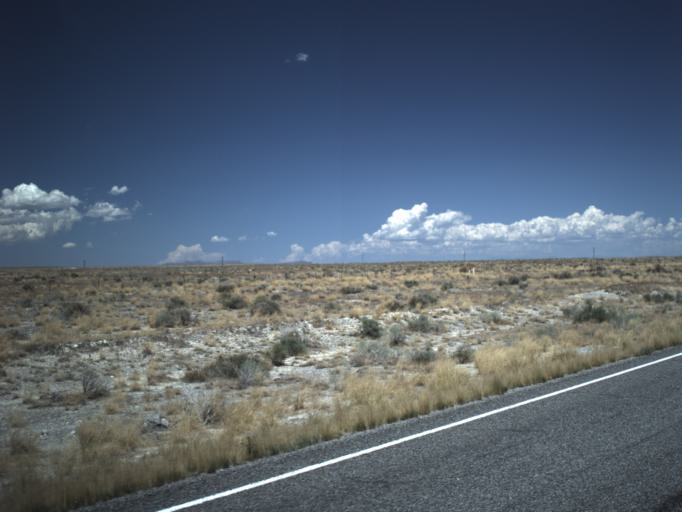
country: US
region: Utah
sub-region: Millard County
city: Delta
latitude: 39.1617
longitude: -113.0496
